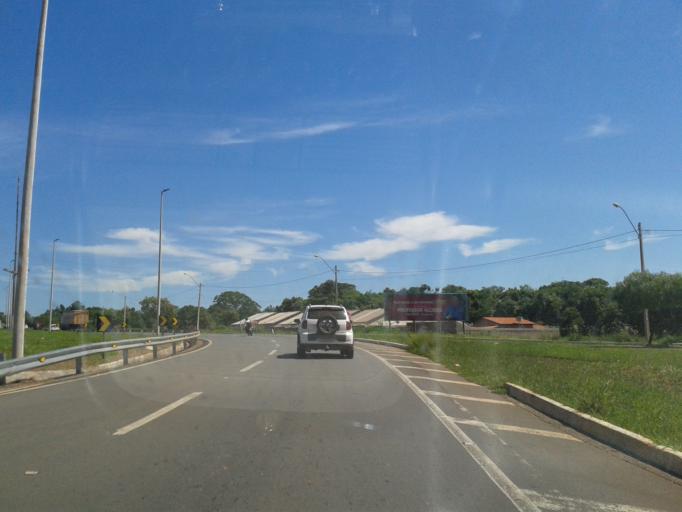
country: BR
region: Goias
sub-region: Bela Vista De Goias
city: Bela Vista de Goias
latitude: -16.9552
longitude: -48.9623
